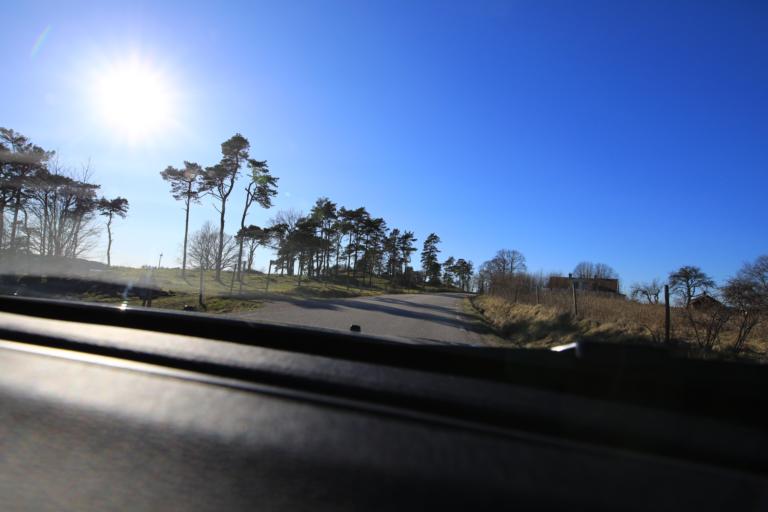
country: SE
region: Halland
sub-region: Varbergs Kommun
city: Tvaaker
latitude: 57.0670
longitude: 12.3820
